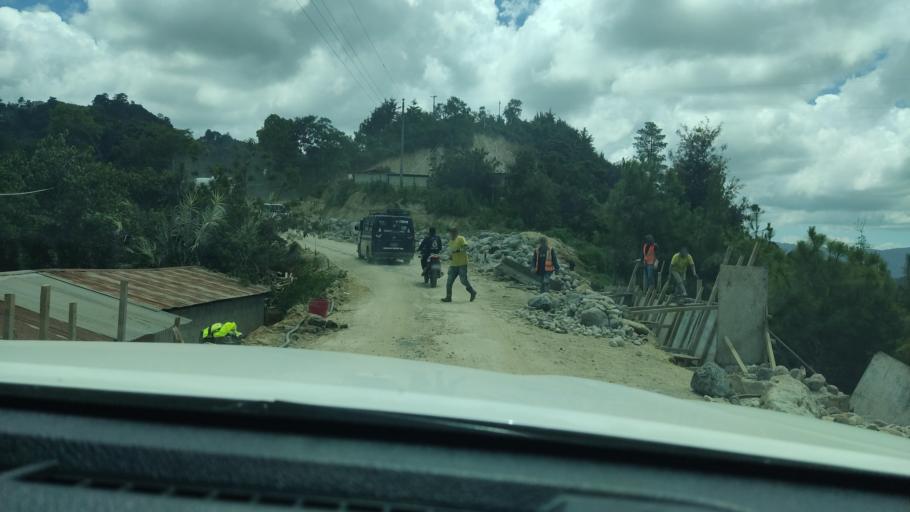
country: GT
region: Chimaltenango
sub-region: Municipio de San Juan Comalapa
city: Comalapa
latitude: 14.7799
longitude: -90.8702
